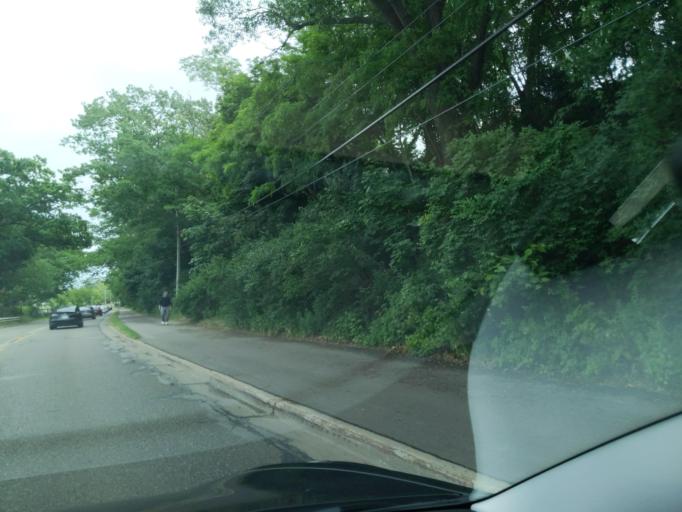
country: US
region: Michigan
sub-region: Muskegon County
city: Roosevelt Park
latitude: 43.2144
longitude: -86.3116
